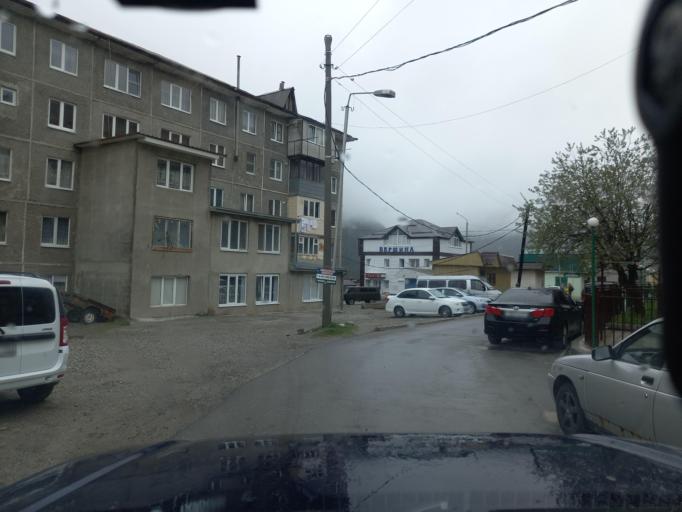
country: RU
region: Kabardino-Balkariya
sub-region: El'brusskiy Rayon
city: El'brus
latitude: 43.2577
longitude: 42.6442
